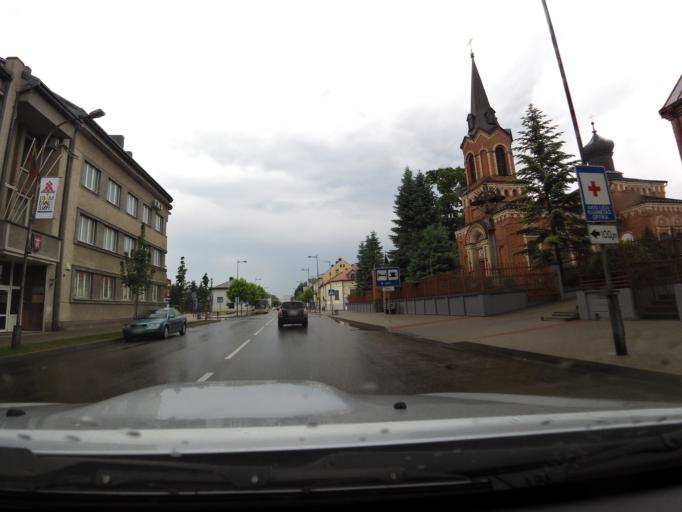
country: LT
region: Marijampoles apskritis
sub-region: Marijampole Municipality
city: Marijampole
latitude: 54.5511
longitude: 23.3483
